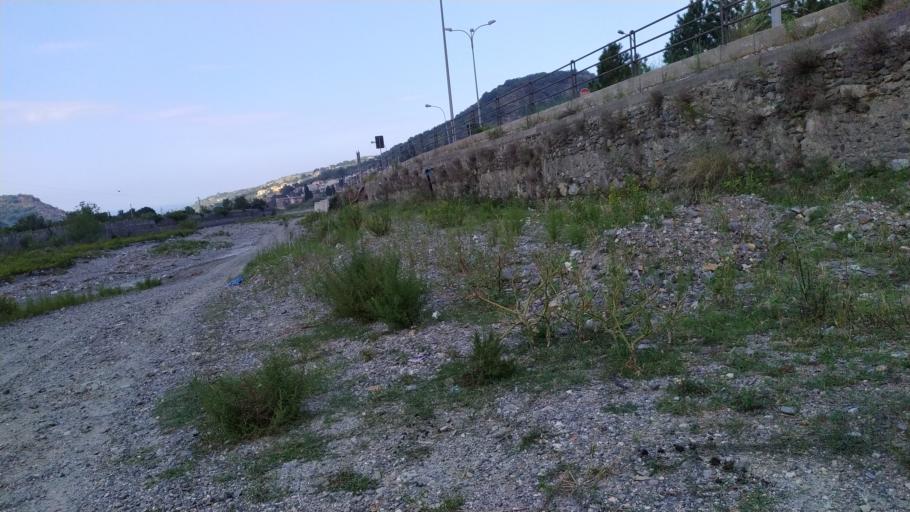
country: IT
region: Sicily
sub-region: Messina
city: Saponara
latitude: 38.1984
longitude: 15.4298
